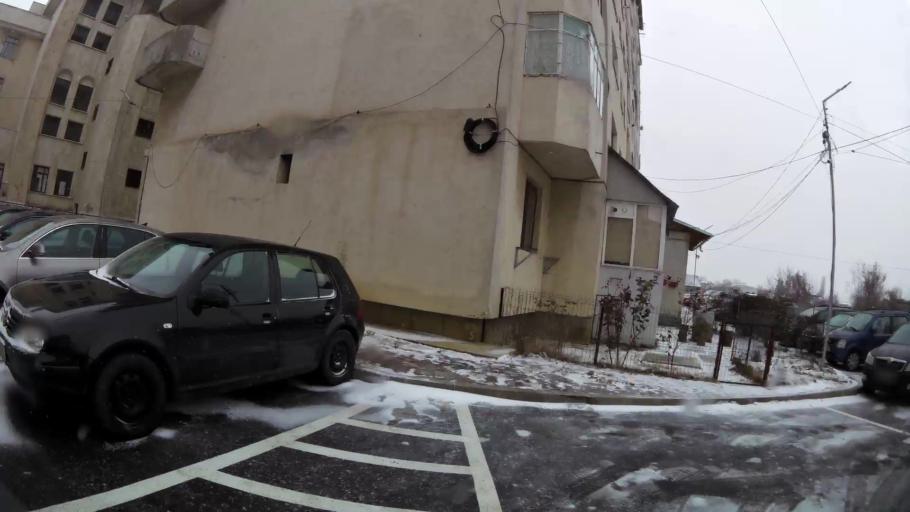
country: RO
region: Dambovita
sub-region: Municipiul Targoviste
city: Targoviste
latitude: 44.9210
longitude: 25.4776
